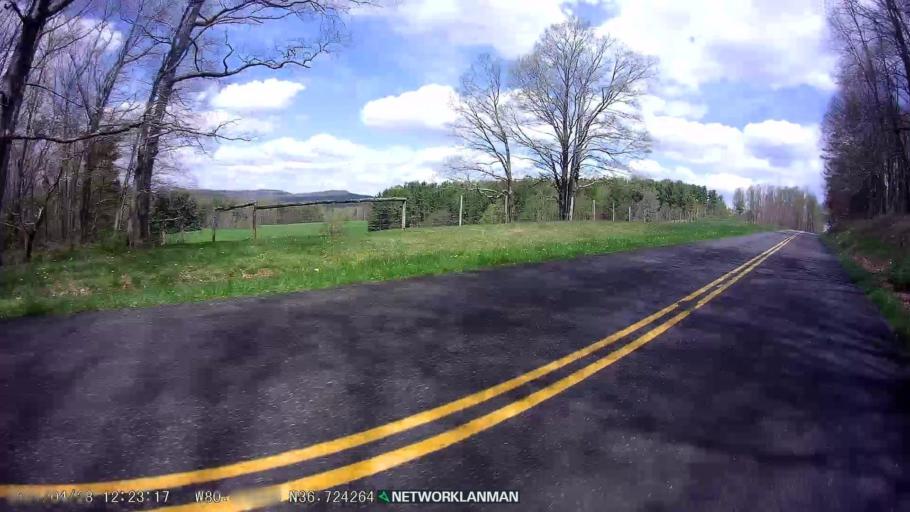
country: US
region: Virginia
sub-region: Patrick County
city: Stuart
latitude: 36.7245
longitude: -80.4141
